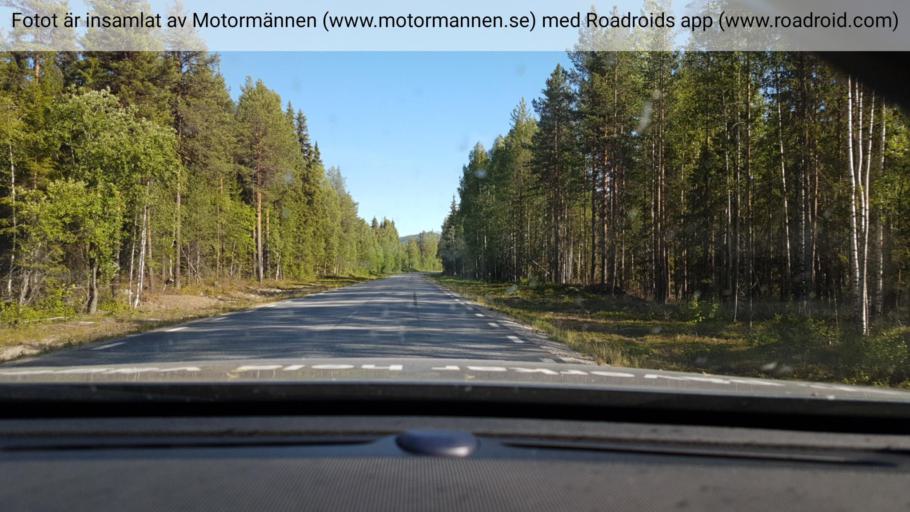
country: SE
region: Vaesterbotten
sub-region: Lycksele Kommun
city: Lycksele
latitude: 64.4496
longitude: 18.9355
